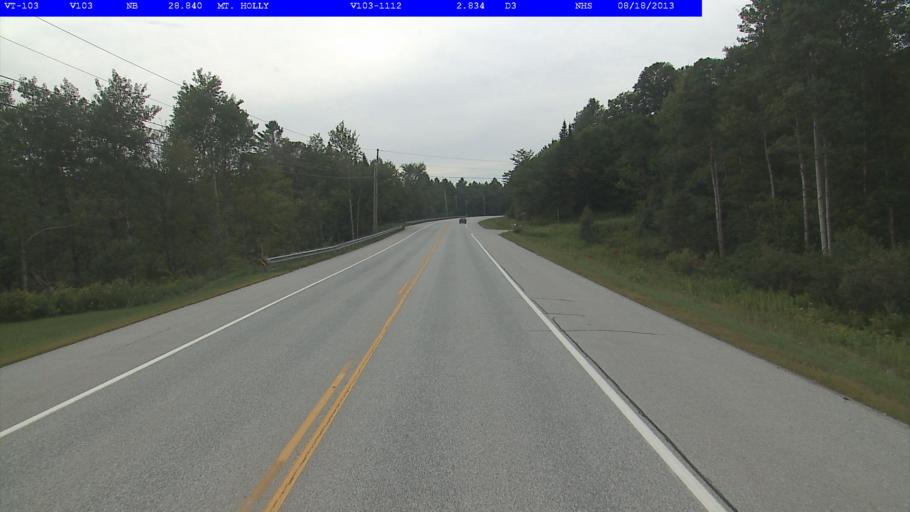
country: US
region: Vermont
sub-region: Rutland County
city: Rutland
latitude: 43.4502
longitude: -72.7830
